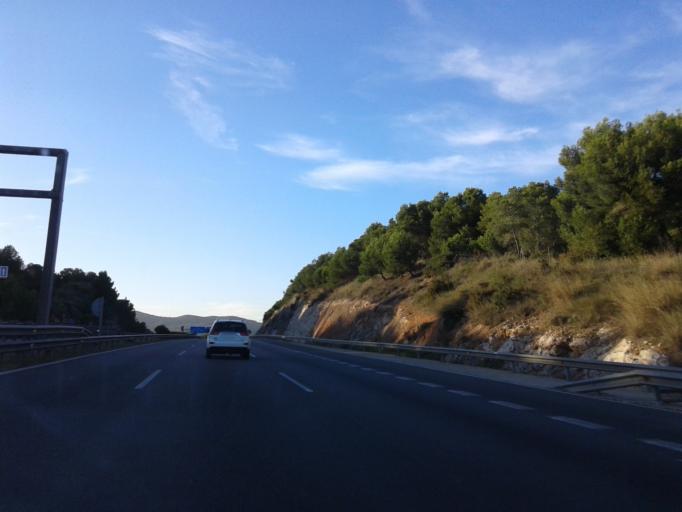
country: ES
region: Catalonia
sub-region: Provincia de Barcelona
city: Sitges
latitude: 41.2495
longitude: 1.8046
